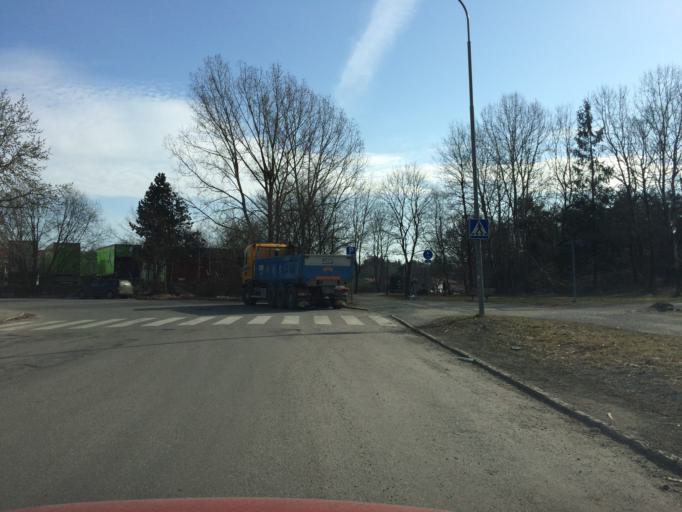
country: SE
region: Stockholm
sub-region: Stockholms Kommun
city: Arsta
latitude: 59.2895
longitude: 18.0088
